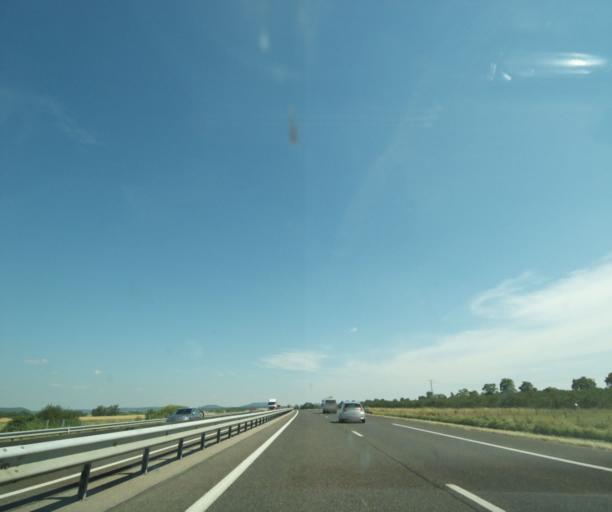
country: FR
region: Lorraine
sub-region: Departement de Meurthe-et-Moselle
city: Blenod-les-Toul
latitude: 48.5864
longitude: 5.8877
